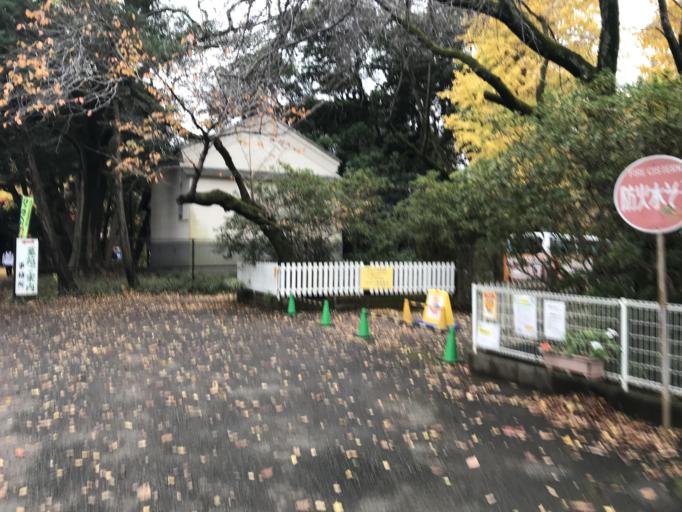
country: JP
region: Chiba
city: Matsudo
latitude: 35.7403
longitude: 139.9073
